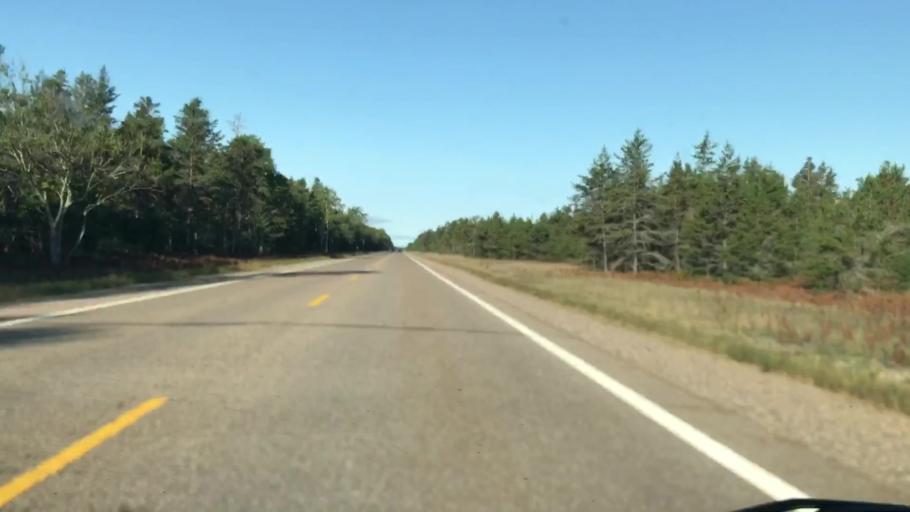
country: US
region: Michigan
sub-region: Mackinac County
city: Saint Ignace
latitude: 46.3585
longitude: -84.8457
